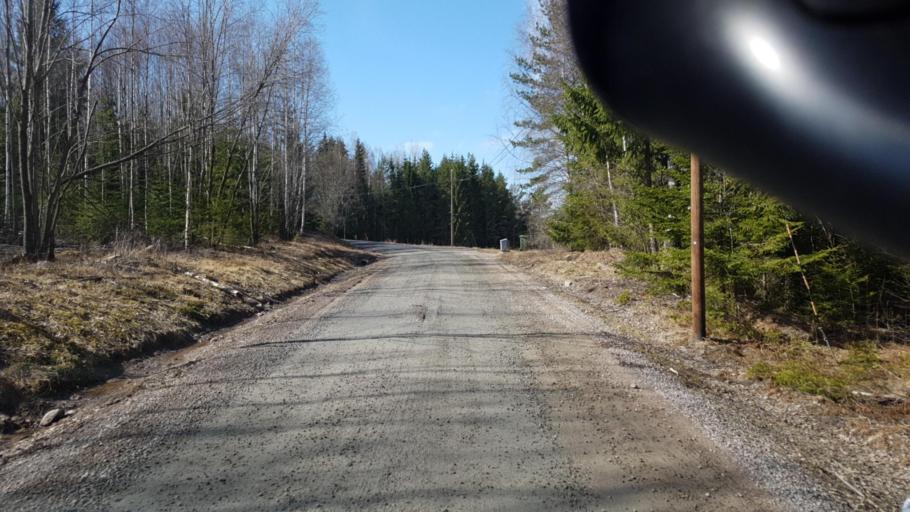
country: SE
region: Vaermland
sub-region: Arvika Kommun
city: Arvika
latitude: 59.6024
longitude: 12.7825
